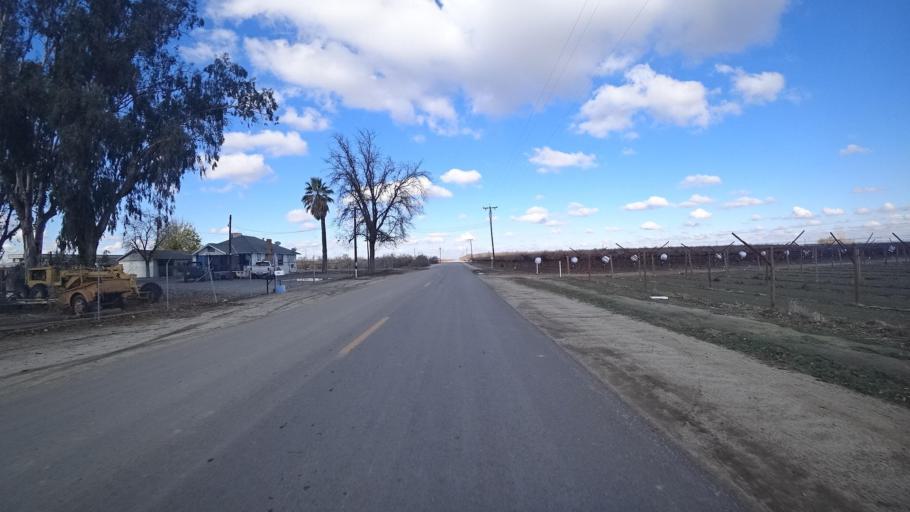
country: US
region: California
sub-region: Kern County
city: Delano
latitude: 35.7444
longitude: -119.3658
